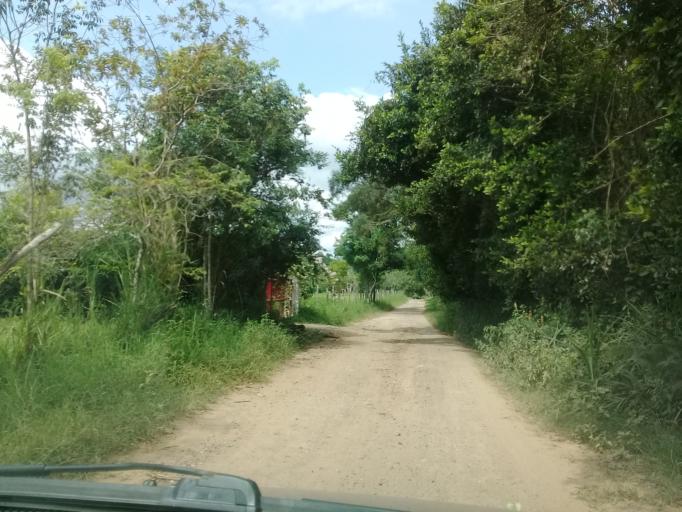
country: CO
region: Cundinamarca
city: Guaduas
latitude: 5.0272
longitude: -74.6078
